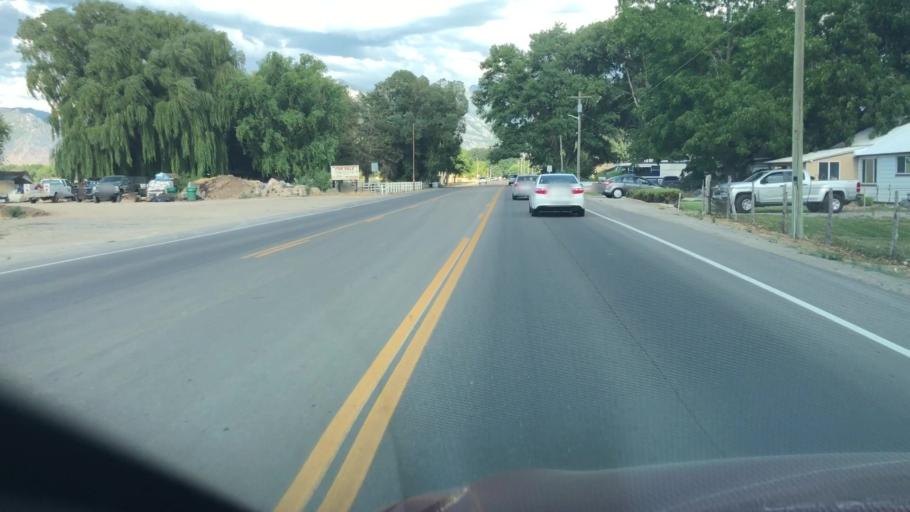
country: US
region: Utah
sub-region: Utah County
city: Lehi
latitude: 40.3872
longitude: -111.8664
